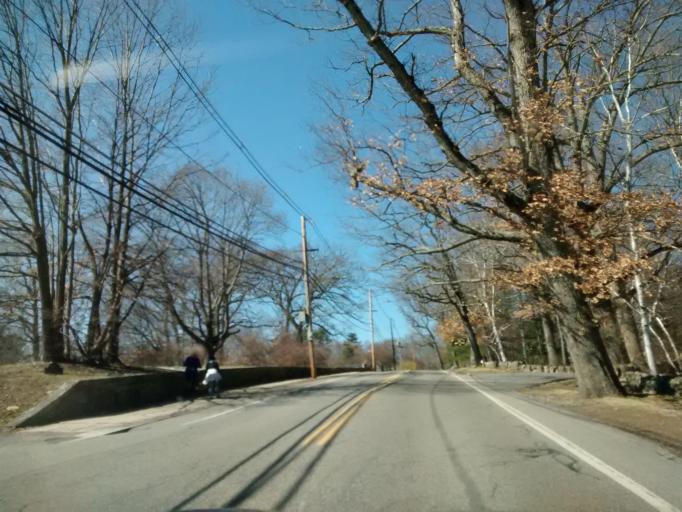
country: US
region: Massachusetts
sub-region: Worcester County
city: Whitinsville
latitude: 42.1130
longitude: -71.6670
